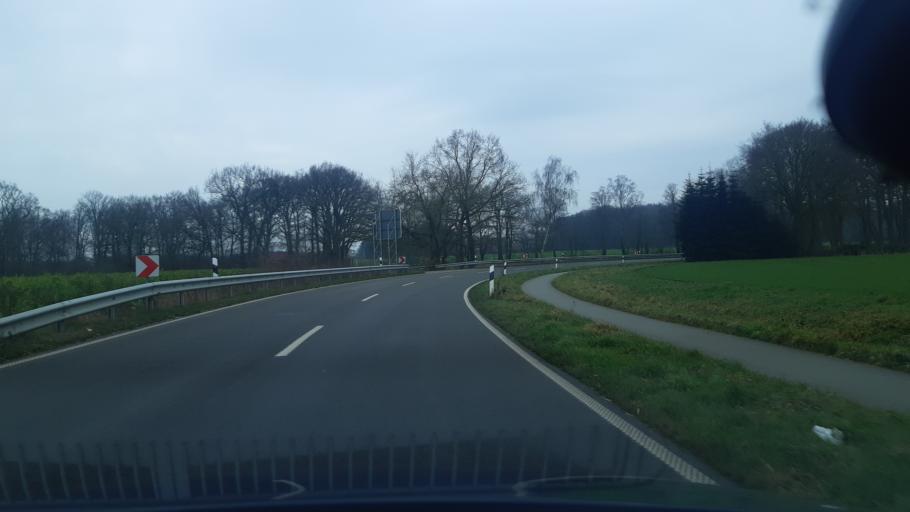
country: DE
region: Lower Saxony
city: Cloppenburg
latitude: 52.8107
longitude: 8.0314
